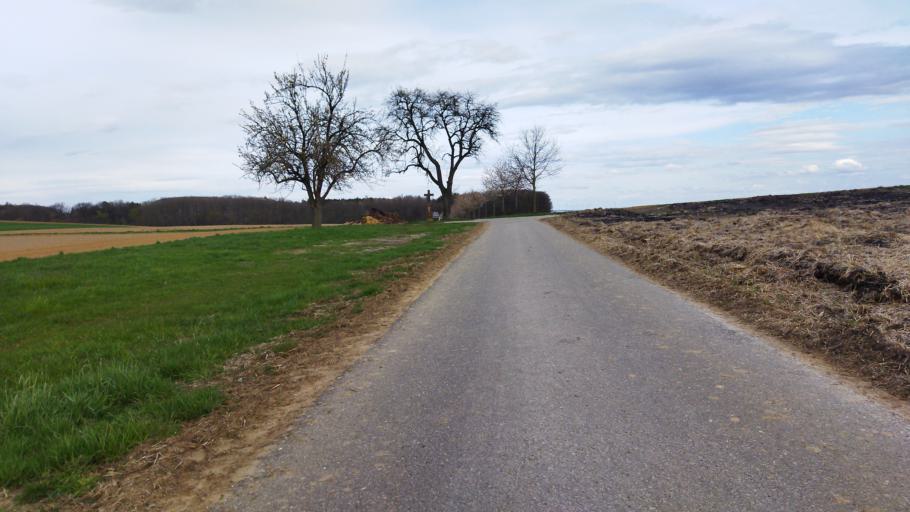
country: DE
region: Baden-Wuerttemberg
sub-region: Regierungsbezirk Stuttgart
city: Gundelsheim
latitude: 49.3020
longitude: 9.2118
